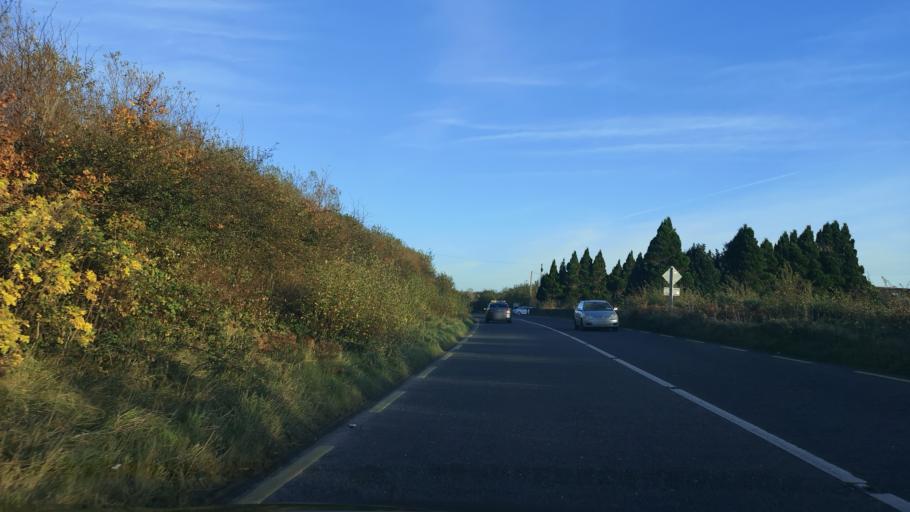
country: IE
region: Connaught
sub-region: County Galway
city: Oughterard
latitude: 53.3997
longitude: -9.2689
